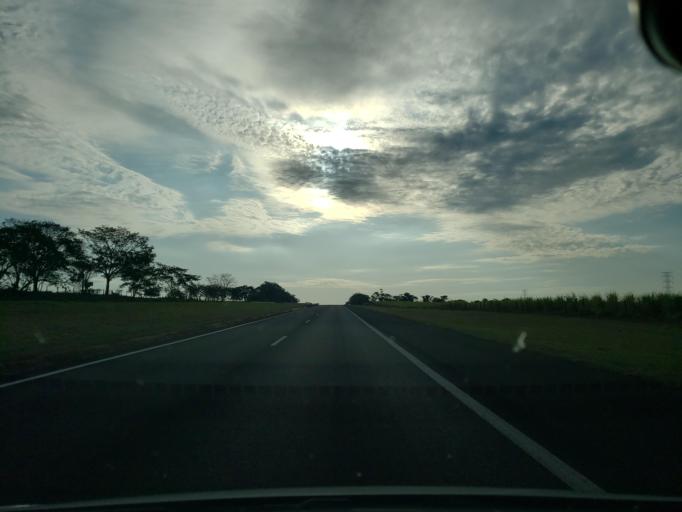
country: BR
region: Sao Paulo
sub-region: Mirandopolis
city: Mirandopolis
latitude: -21.0959
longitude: -51.0474
